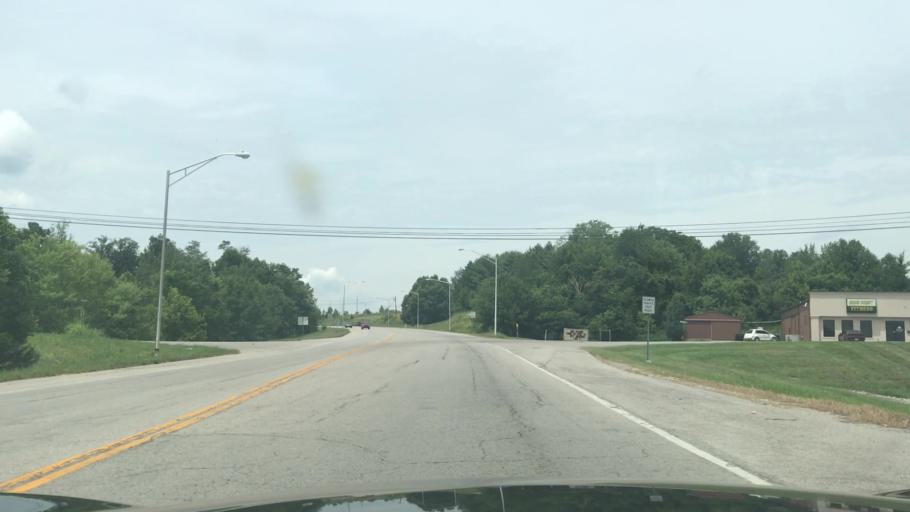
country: US
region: Kentucky
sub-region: Green County
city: Greensburg
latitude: 37.2717
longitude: -85.4976
